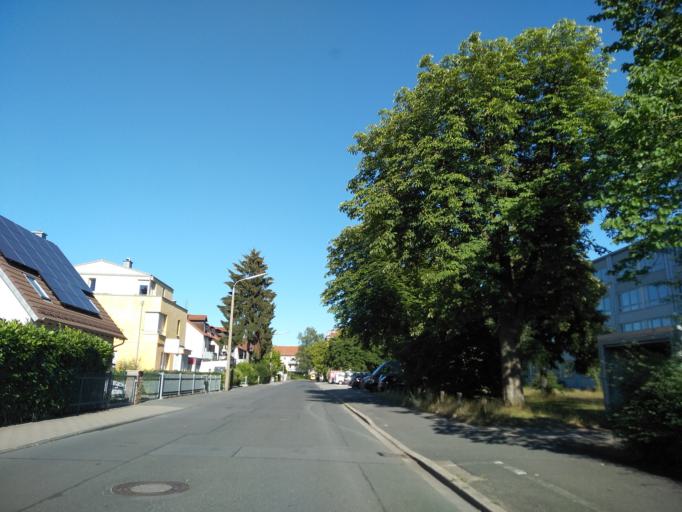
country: DE
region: Bavaria
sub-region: Regierungsbezirk Mittelfranken
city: Erlangen
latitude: 49.5981
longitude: 11.0271
